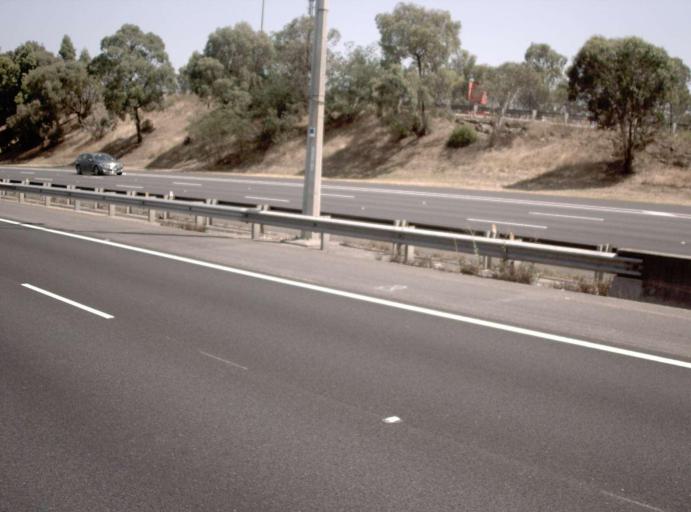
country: AU
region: Victoria
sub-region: Manningham
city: Bulleen
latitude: -37.7800
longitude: 145.0806
